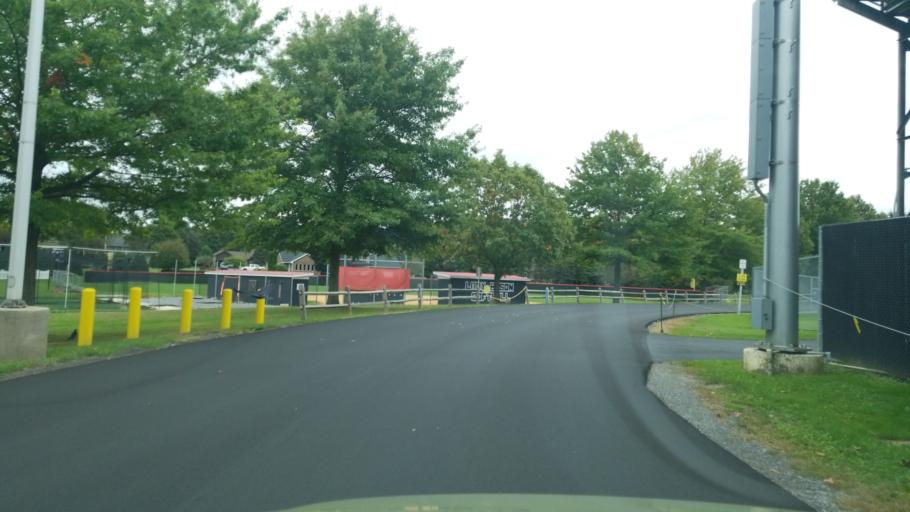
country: US
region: Pennsylvania
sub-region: Clearfield County
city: Hyde
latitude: 40.9920
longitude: -78.4801
